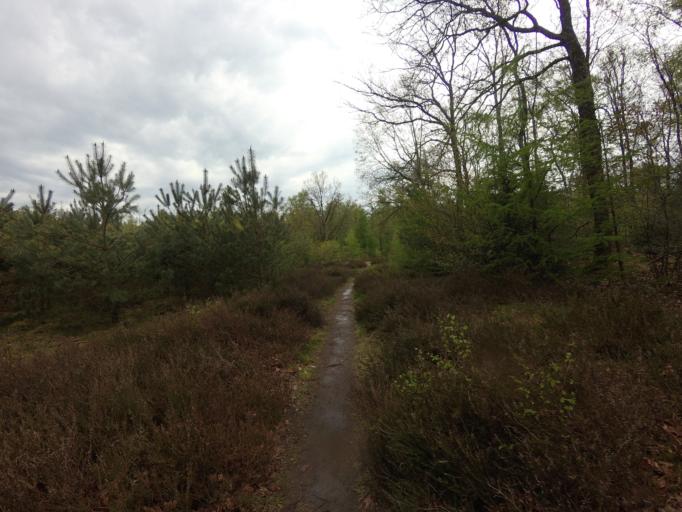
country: NL
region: Utrecht
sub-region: Gemeente Utrechtse Heuvelrug
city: Amerongen
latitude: 51.9965
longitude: 5.4862
